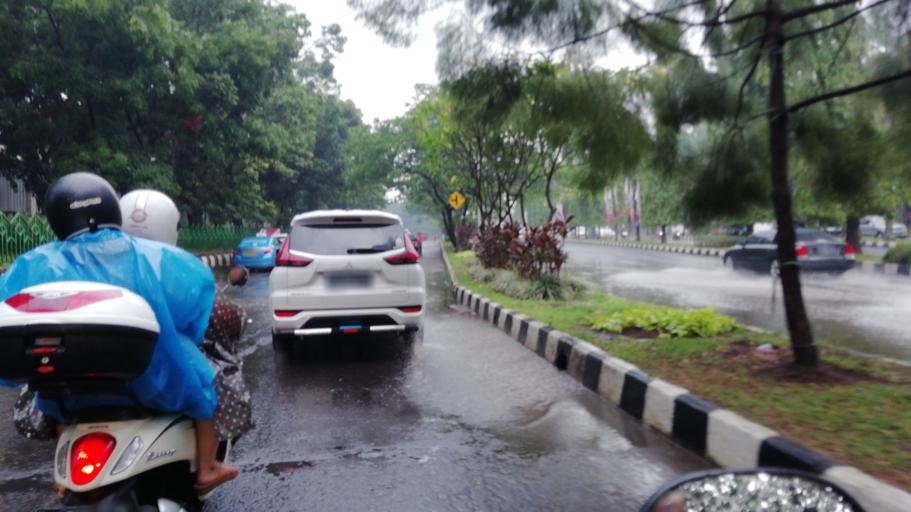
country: ID
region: West Java
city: Cibinong
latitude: -6.4810
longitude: 106.8228
